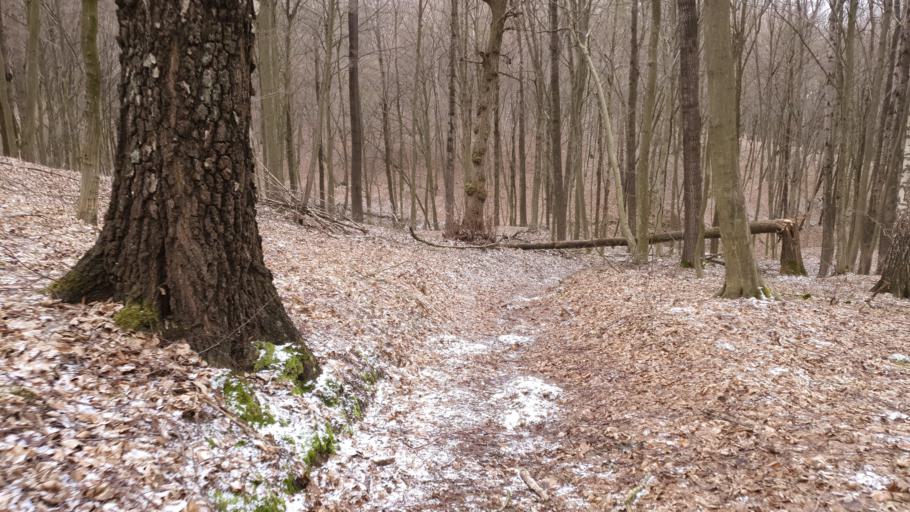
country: PL
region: Lublin Voivodeship
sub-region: Powiat pulawski
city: Naleczow
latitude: 51.2806
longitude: 22.2083
